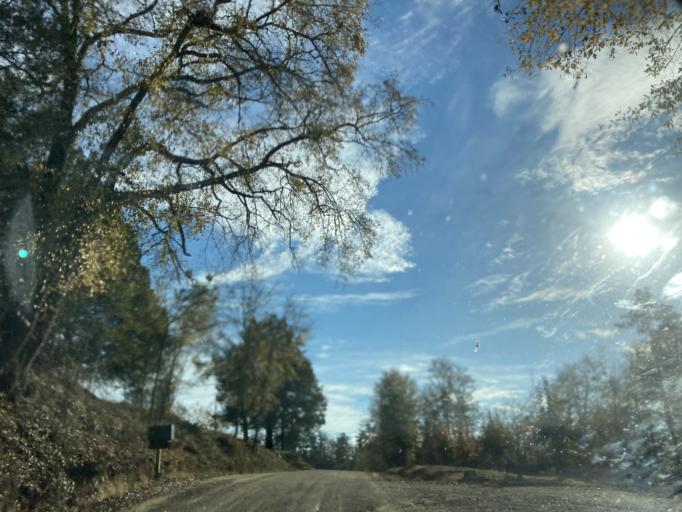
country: US
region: Georgia
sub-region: Jones County
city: Gray
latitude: 32.9014
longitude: -83.4907
